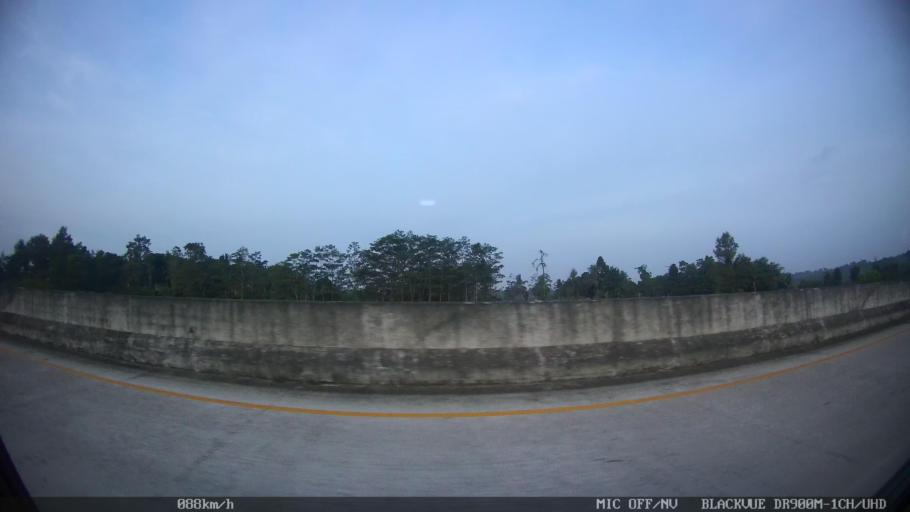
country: ID
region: Lampung
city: Penengahan
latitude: -5.7670
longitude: 105.7149
